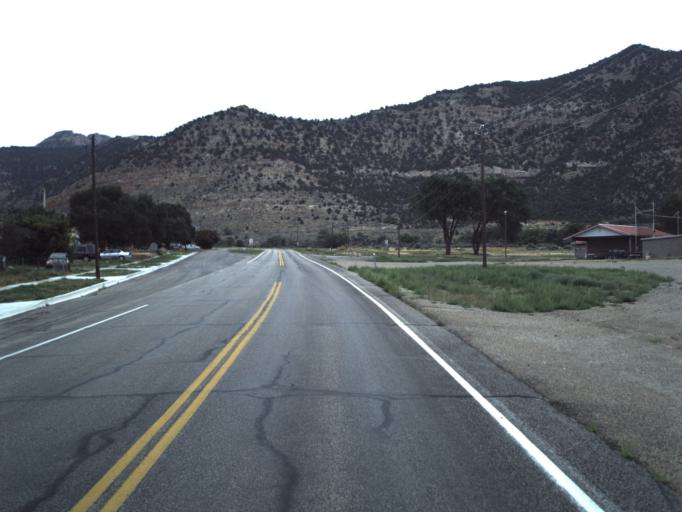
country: US
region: Utah
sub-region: Carbon County
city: East Carbon City
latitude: 39.5500
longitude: -110.3898
